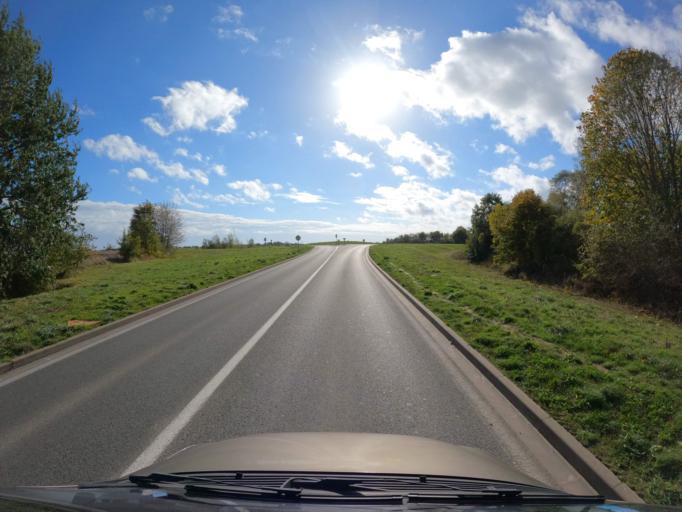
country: FR
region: Ile-de-France
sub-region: Departement de Seine-et-Marne
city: Coupvray
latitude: 48.8843
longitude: 2.8067
